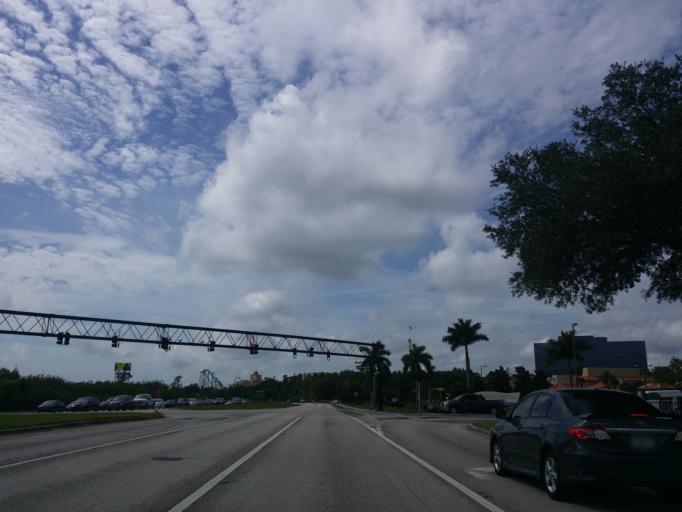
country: US
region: Florida
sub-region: Orange County
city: Williamsburg
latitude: 28.4199
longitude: -81.4601
